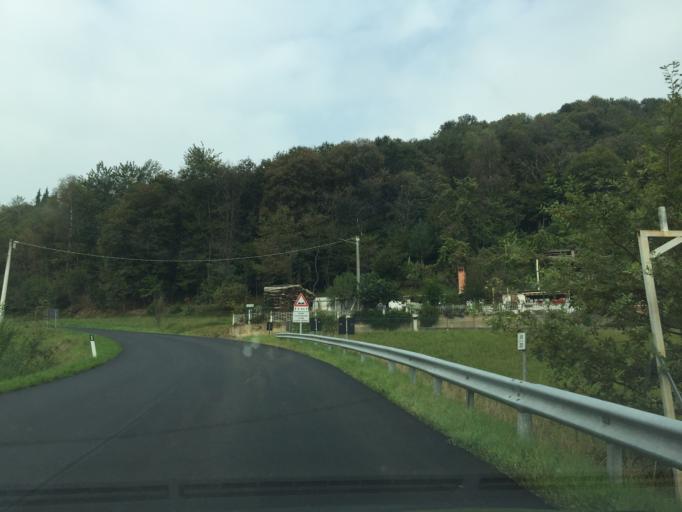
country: IT
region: Piedmont
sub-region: Provincia di Cuneo
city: Roccaforte Mondovi
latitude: 44.3107
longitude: 7.7159
